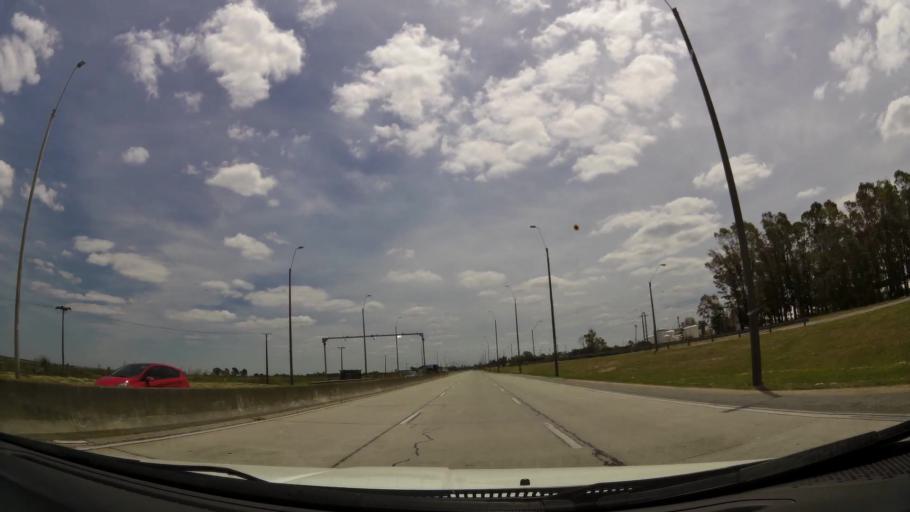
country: UY
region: San Jose
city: Delta del Tigre
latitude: -34.7743
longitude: -56.3794
